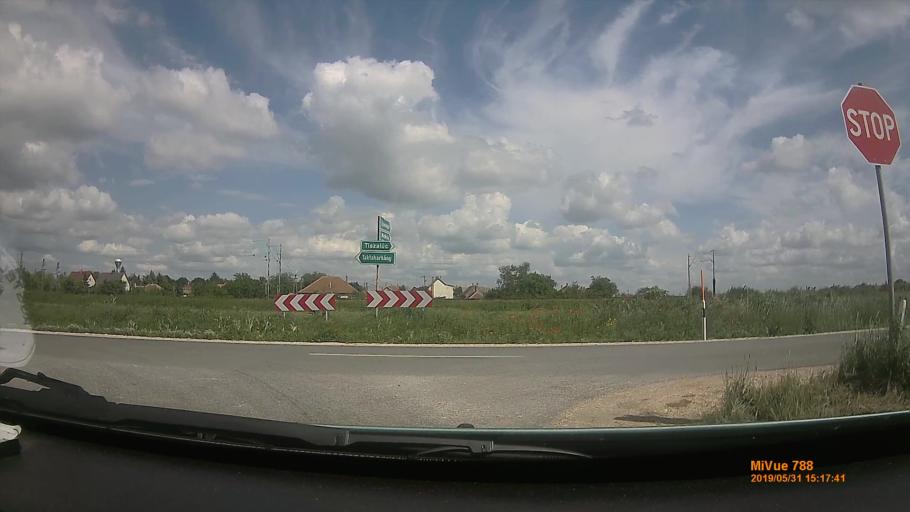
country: HU
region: Borsod-Abauj-Zemplen
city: Taktaharkany
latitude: 48.0827
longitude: 21.1225
